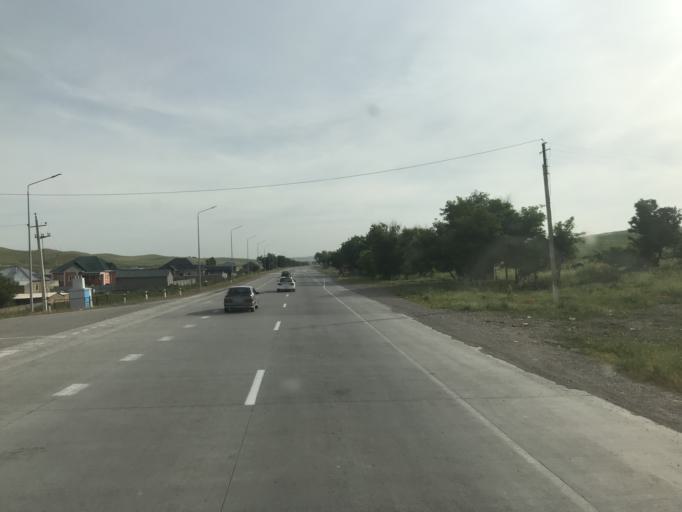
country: KZ
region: Ongtustik Qazaqstan
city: Qazyqurt
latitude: 41.9058
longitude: 69.4650
